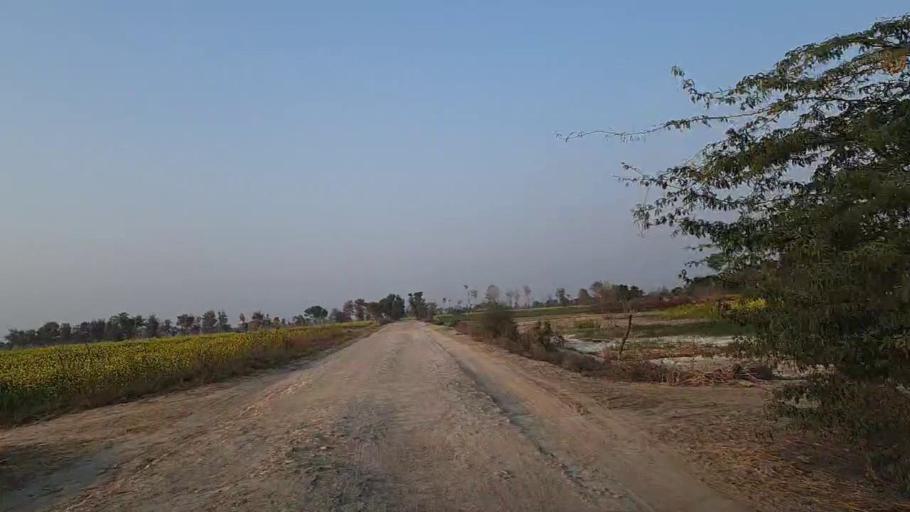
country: PK
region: Sindh
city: Daur
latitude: 26.4277
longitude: 68.3859
